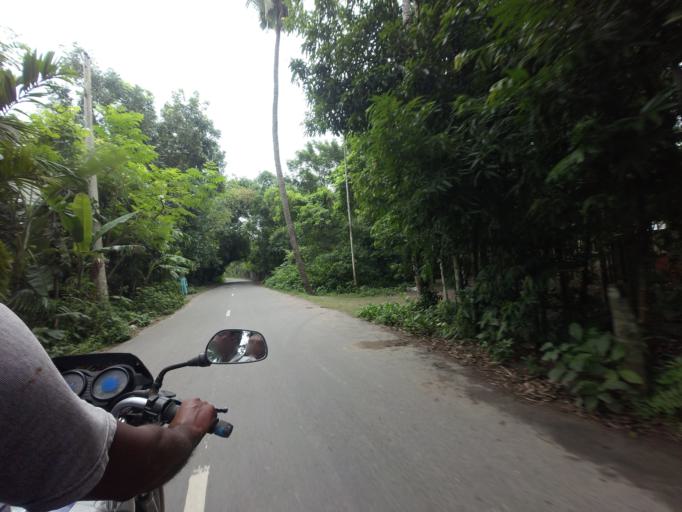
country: BD
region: Khulna
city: Kalia
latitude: 23.1360
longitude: 89.6441
